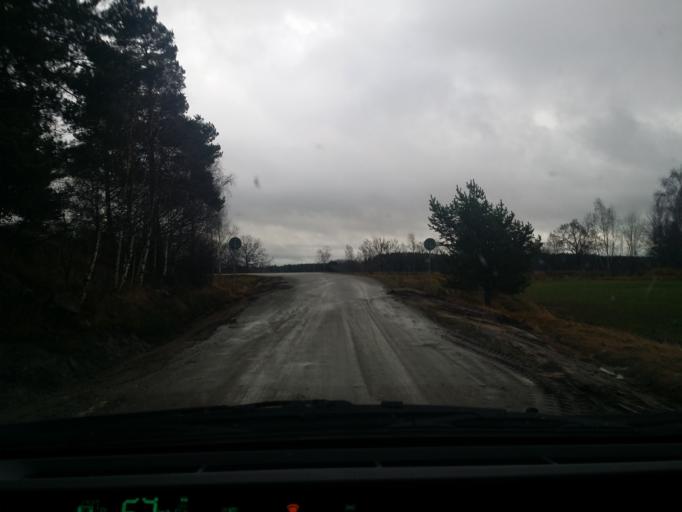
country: SE
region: Vaestmanland
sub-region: Vasteras
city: Skultuna
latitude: 59.7812
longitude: 16.4605
